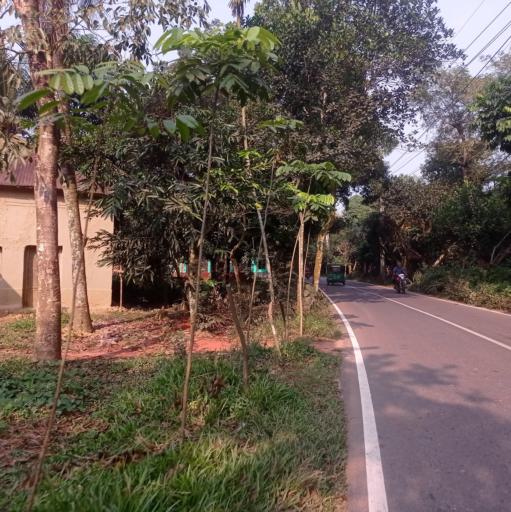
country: BD
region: Dhaka
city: Bhairab Bazar
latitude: 24.0741
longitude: 90.8457
